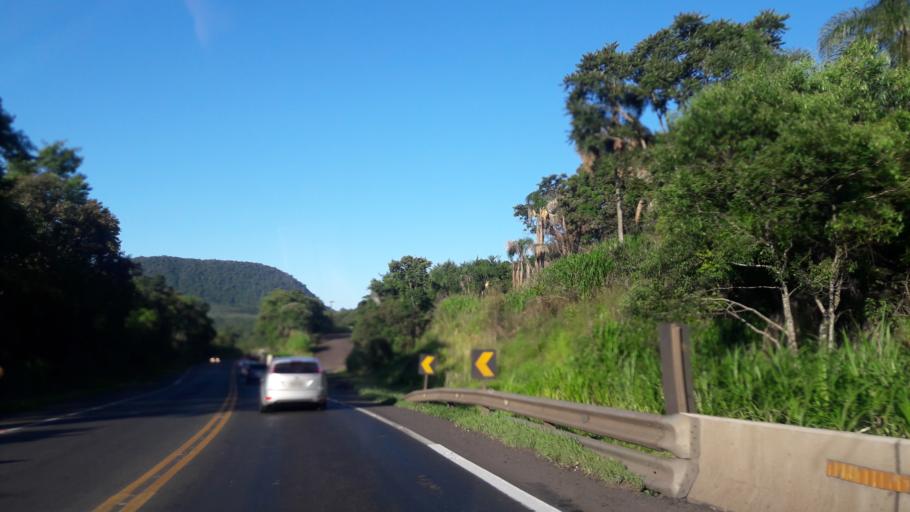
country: BR
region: Parana
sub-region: Prudentopolis
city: Prudentopolis
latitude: -25.3236
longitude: -51.1918
